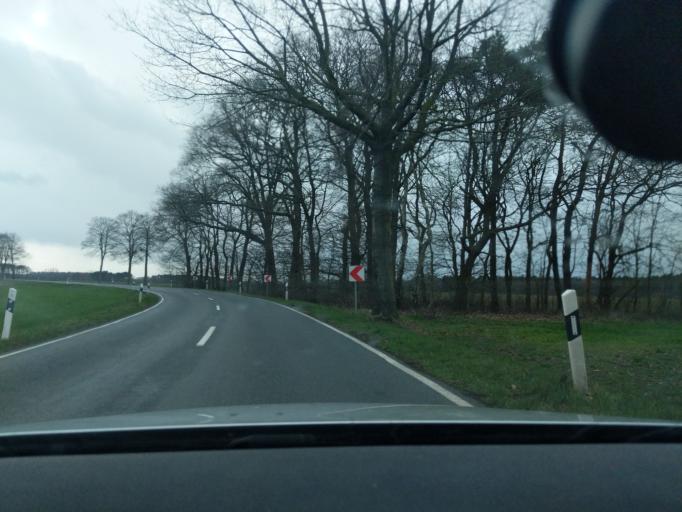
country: DE
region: Lower Saxony
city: Bliedersdorf
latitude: 53.5023
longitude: 9.5410
